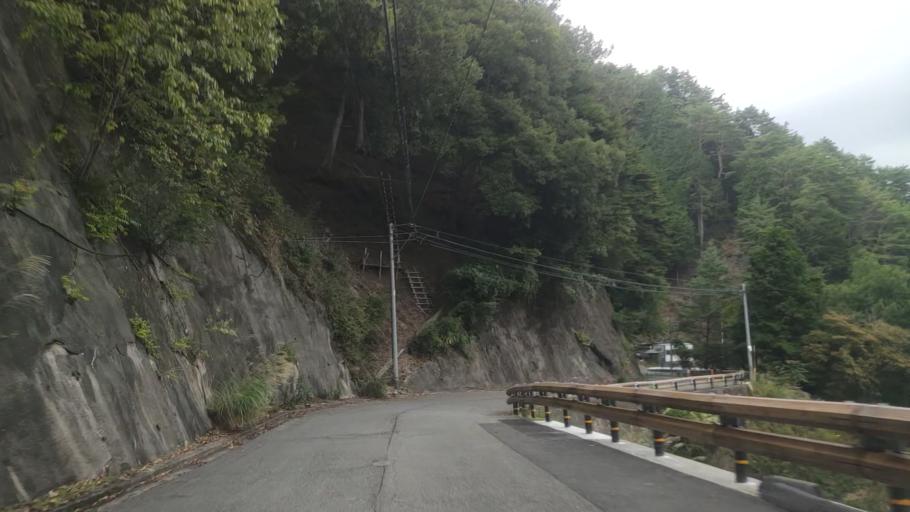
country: JP
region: Wakayama
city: Koya
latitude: 34.2203
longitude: 135.6130
